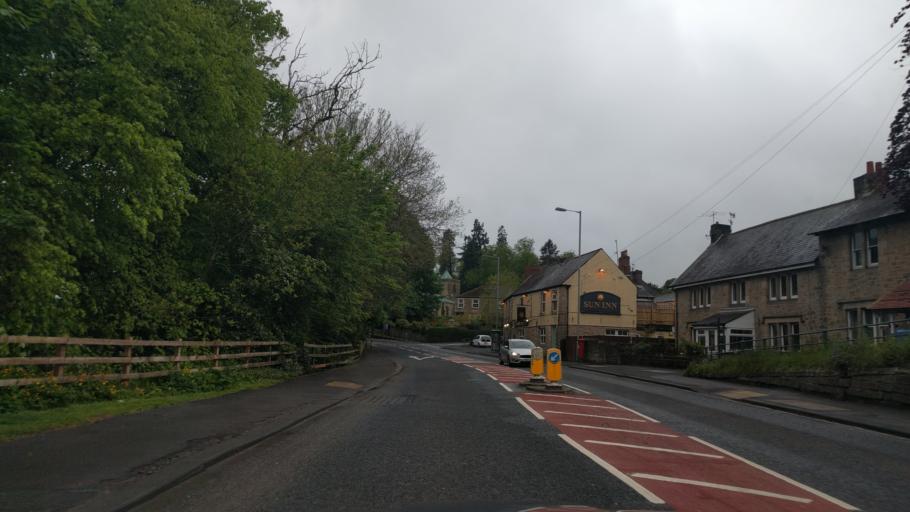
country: GB
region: England
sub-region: Northumberland
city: Morpeth
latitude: 55.1611
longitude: -1.6908
